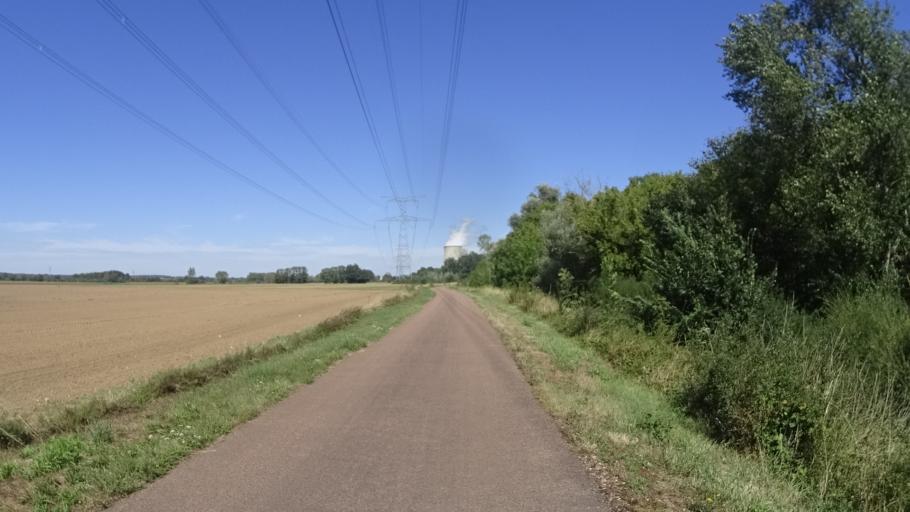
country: FR
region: Centre
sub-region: Departement du Cher
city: Lere
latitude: 47.4920
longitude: 2.8918
